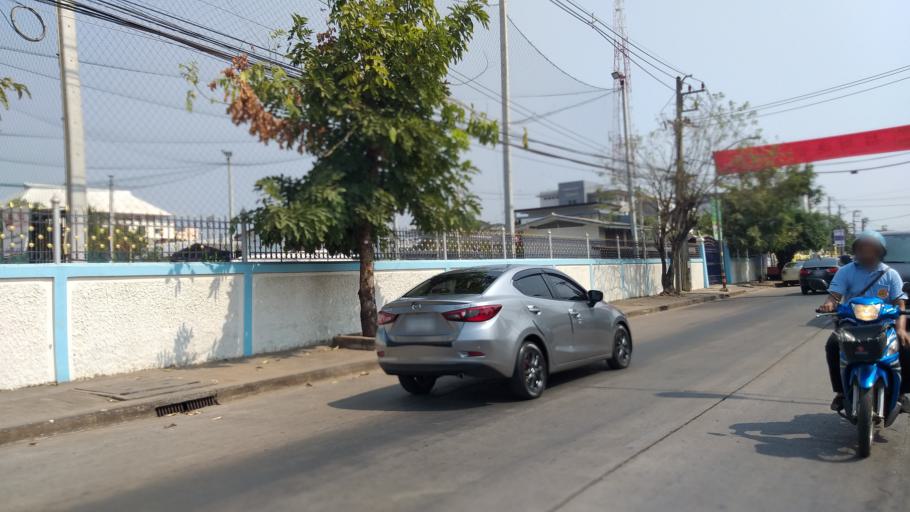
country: TH
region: Changwat Udon Thani
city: Udon Thani
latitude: 17.4063
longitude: 102.7789
